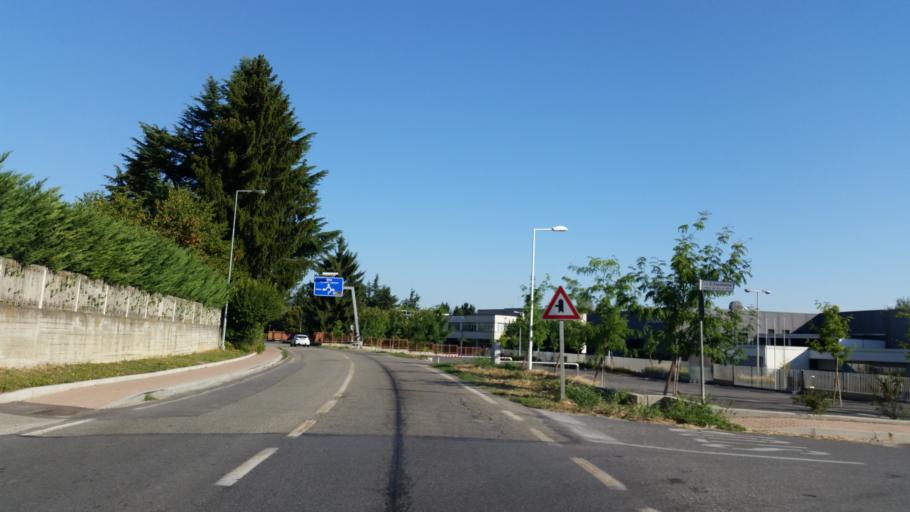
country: IT
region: Piedmont
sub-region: Provincia di Cuneo
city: Roddi
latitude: 44.6806
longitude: 7.9846
